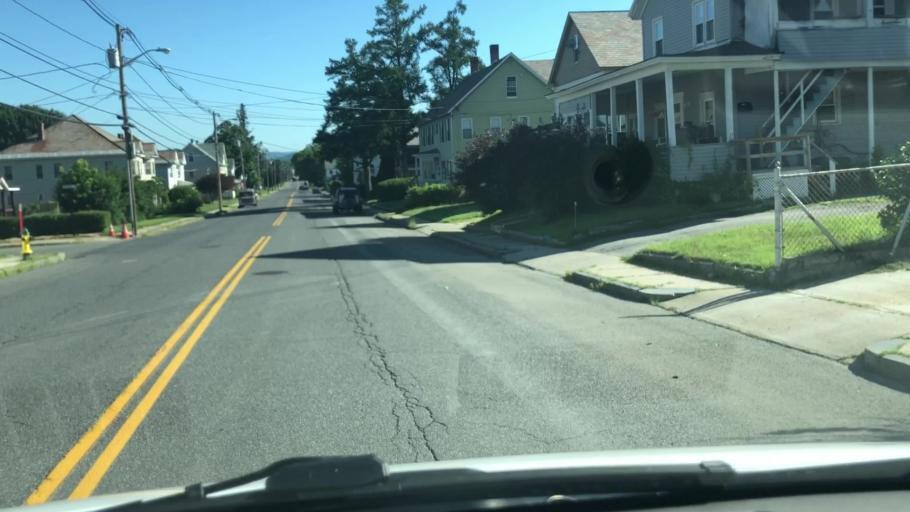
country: US
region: Massachusetts
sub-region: Berkshire County
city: Adams
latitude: 42.6280
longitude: -73.1119
